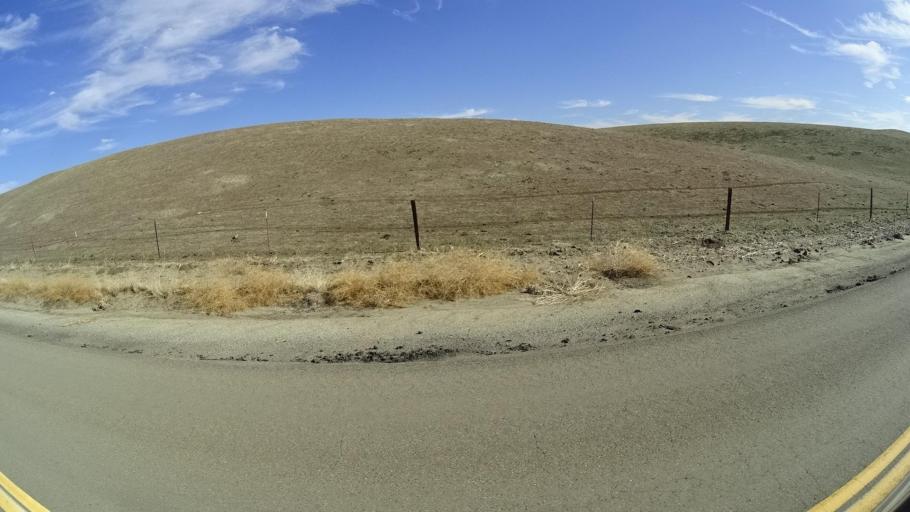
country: US
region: California
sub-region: Kern County
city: Oildale
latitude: 35.6123
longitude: -118.9442
